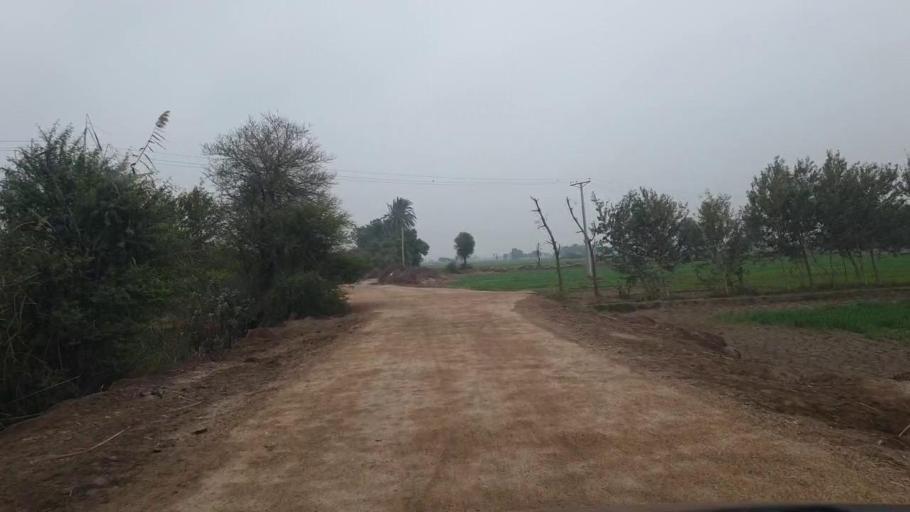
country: PK
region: Sindh
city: Tando Adam
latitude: 25.8463
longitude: 68.6842
